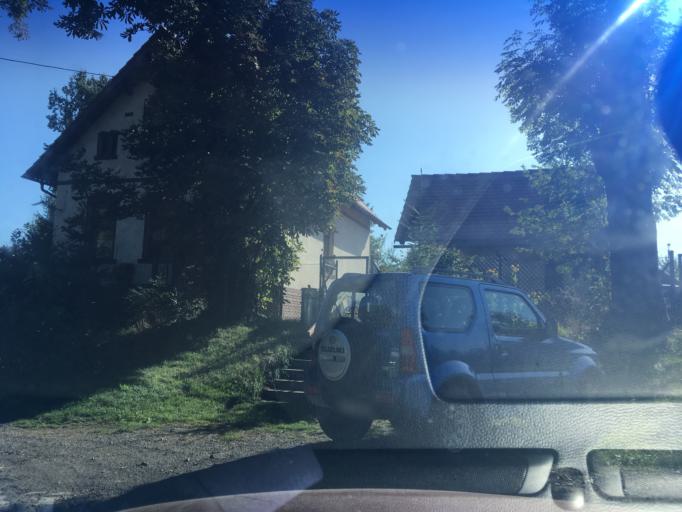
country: PL
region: Lower Silesian Voivodeship
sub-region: Powiat lubanski
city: Swieradow-Zdroj
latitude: 50.9524
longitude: 15.3076
